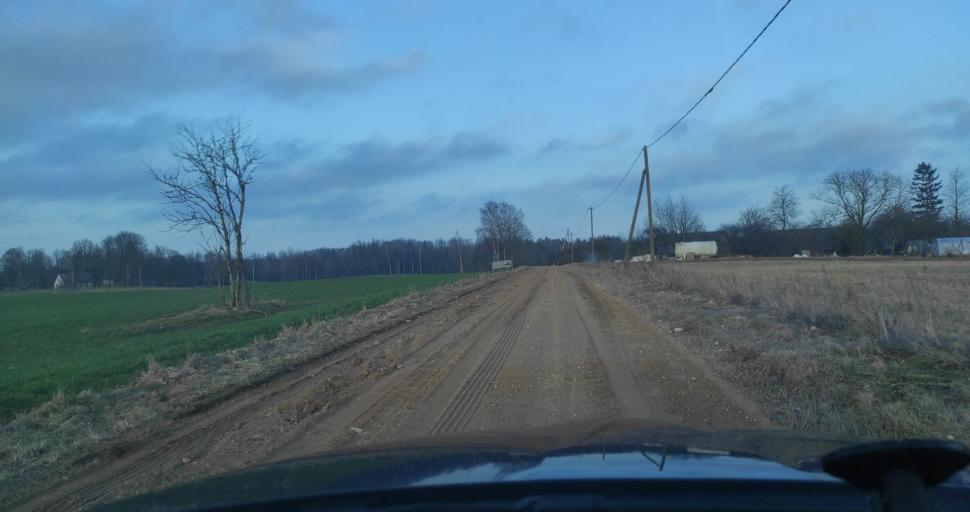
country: LV
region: Aizpute
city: Aizpute
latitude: 56.7995
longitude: 21.8009
